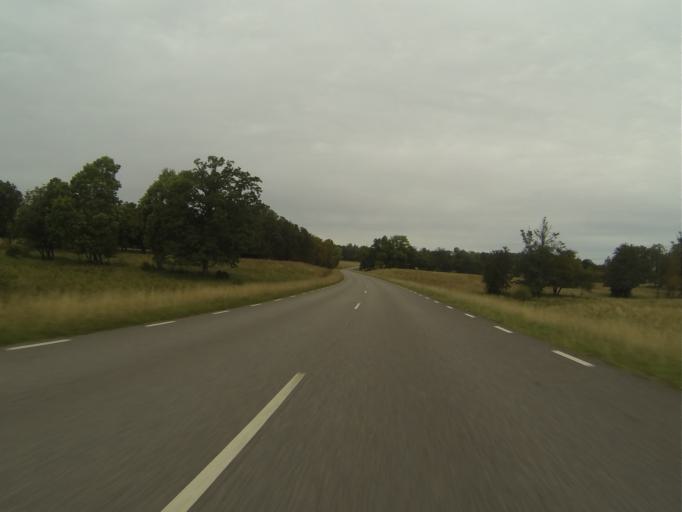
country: SE
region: Skane
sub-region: Lunds Kommun
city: Veberod
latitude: 55.6888
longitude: 13.4240
